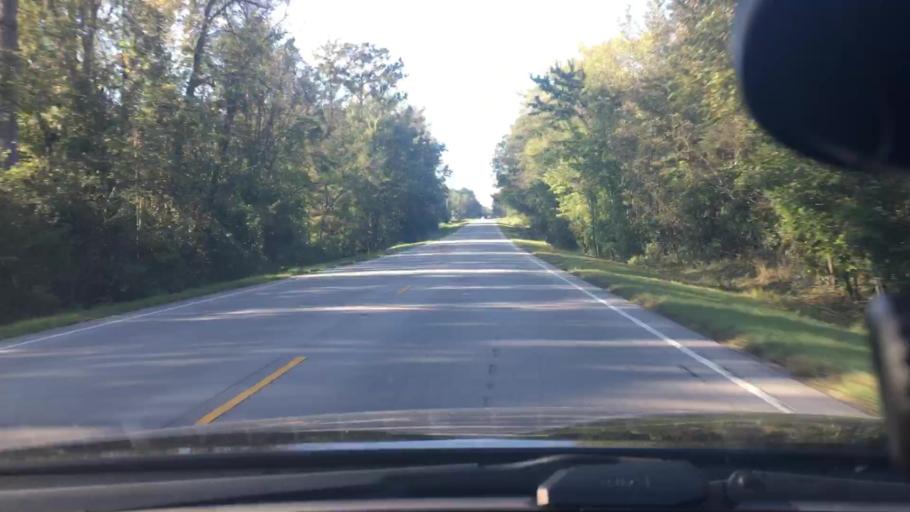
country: US
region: North Carolina
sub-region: Craven County
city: Vanceboro
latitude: 35.3129
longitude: -77.1401
